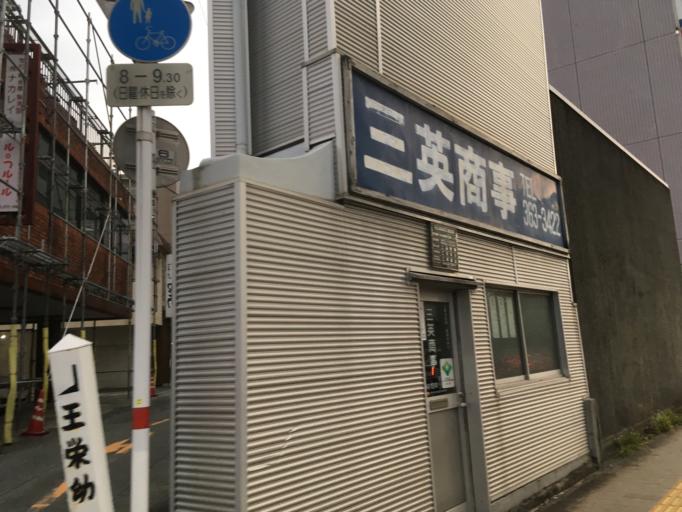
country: JP
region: Kumamoto
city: Kumamoto
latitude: 32.7991
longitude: 130.7181
